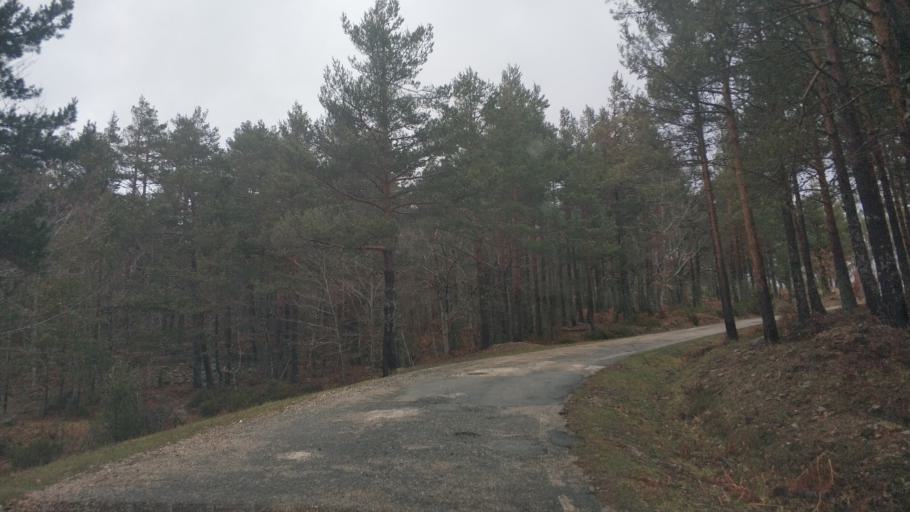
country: ES
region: Castille and Leon
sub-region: Provincia de Burgos
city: Neila
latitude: 42.0434
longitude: -3.0159
